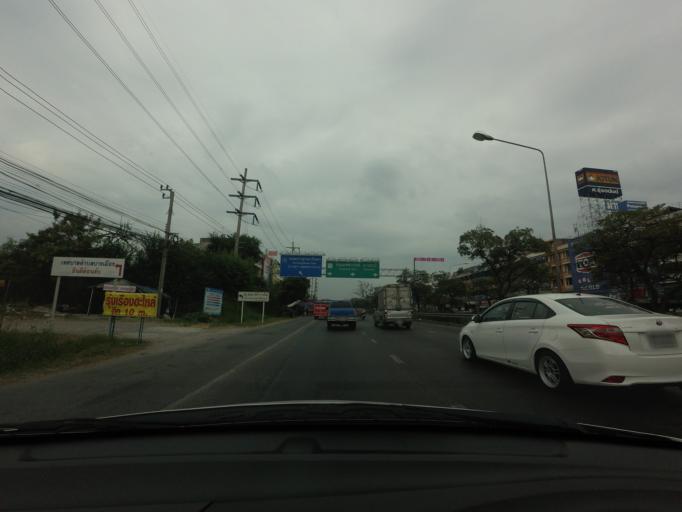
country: TH
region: Samut Prakan
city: Samut Prakan
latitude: 13.6110
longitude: 100.6179
